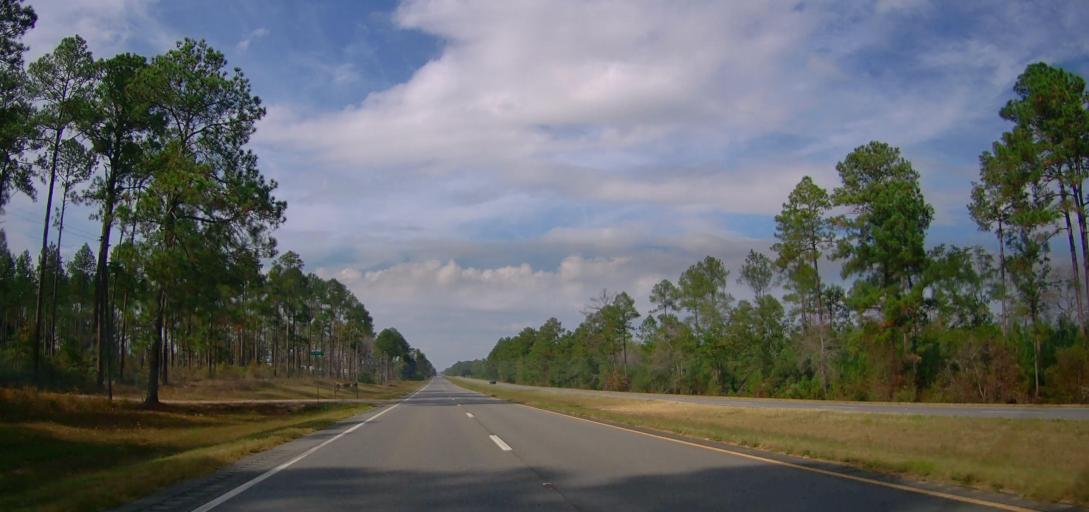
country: US
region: Georgia
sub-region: Thomas County
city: Thomasville
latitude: 30.9548
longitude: -84.0267
